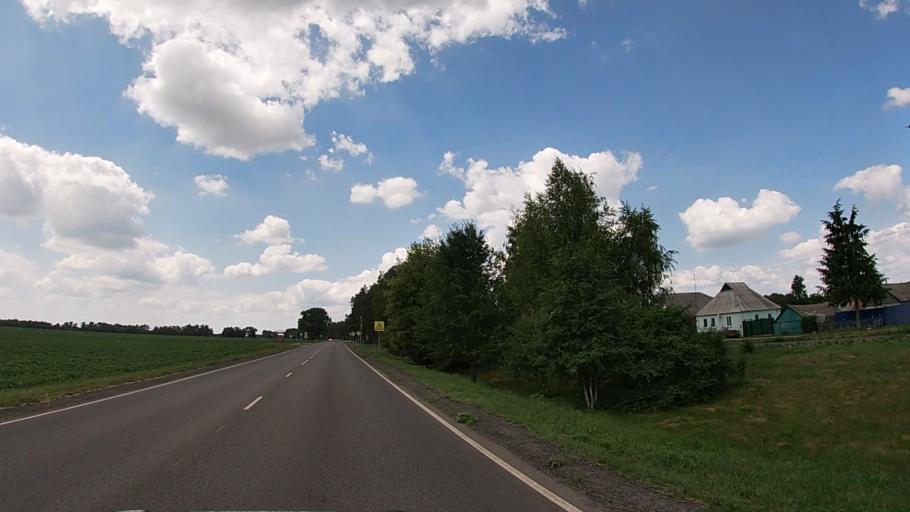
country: RU
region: Belgorod
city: Golovchino
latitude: 50.5095
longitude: 35.7530
